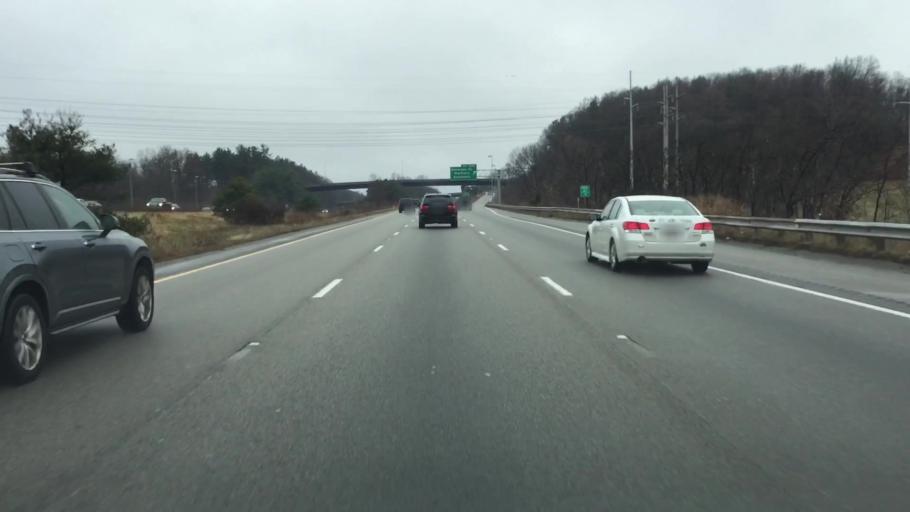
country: US
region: Massachusetts
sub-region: Middlesex County
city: Marlborough
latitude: 42.3162
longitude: -71.5689
